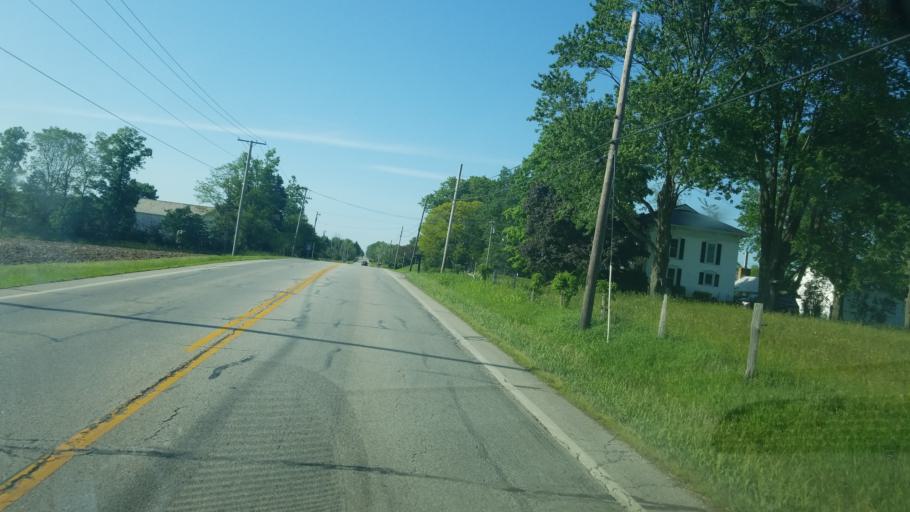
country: US
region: Ohio
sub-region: Medina County
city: Seville
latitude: 41.0462
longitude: -81.8644
